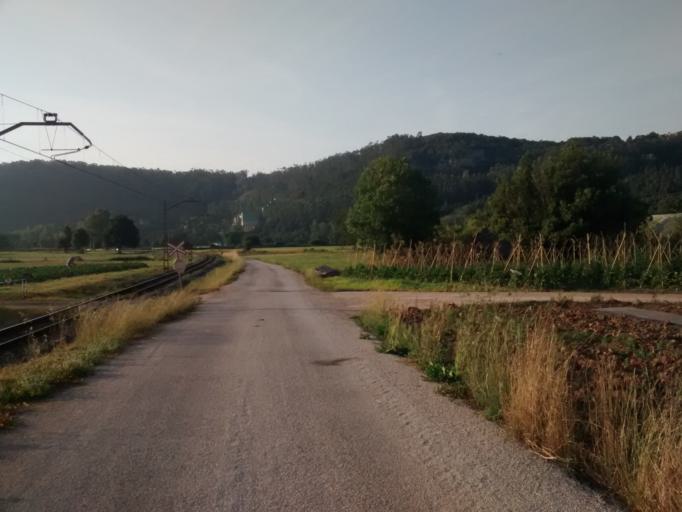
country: ES
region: Cantabria
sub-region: Provincia de Cantabria
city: Entrambasaguas
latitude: 43.3718
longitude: -3.7134
